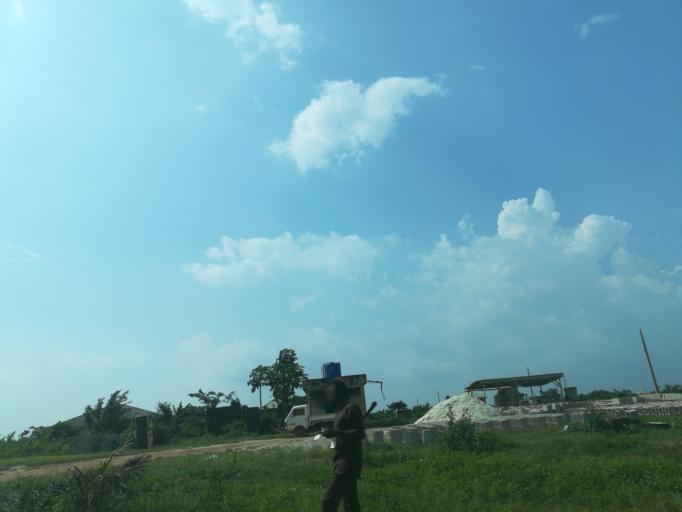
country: NG
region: Lagos
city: Ikorodu
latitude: 6.6185
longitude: 3.6523
